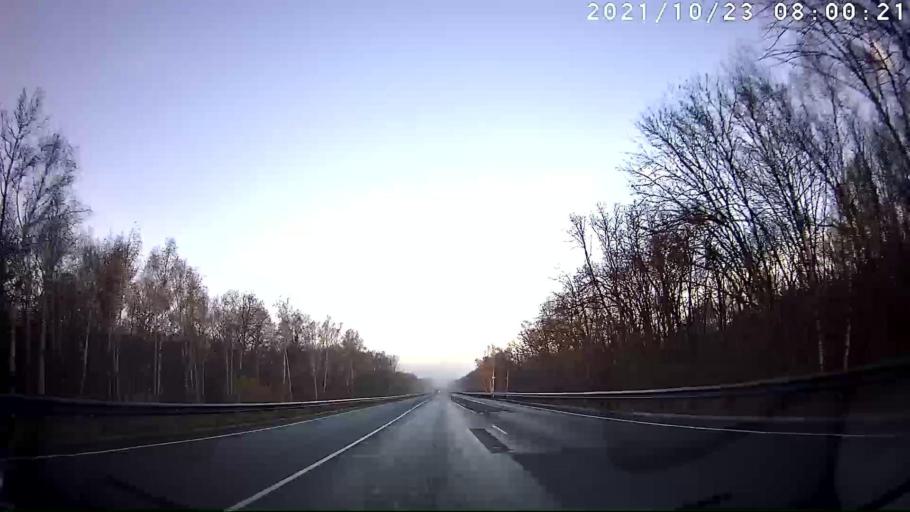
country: RU
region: Saratov
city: Vol'sk
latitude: 52.1064
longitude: 47.4274
